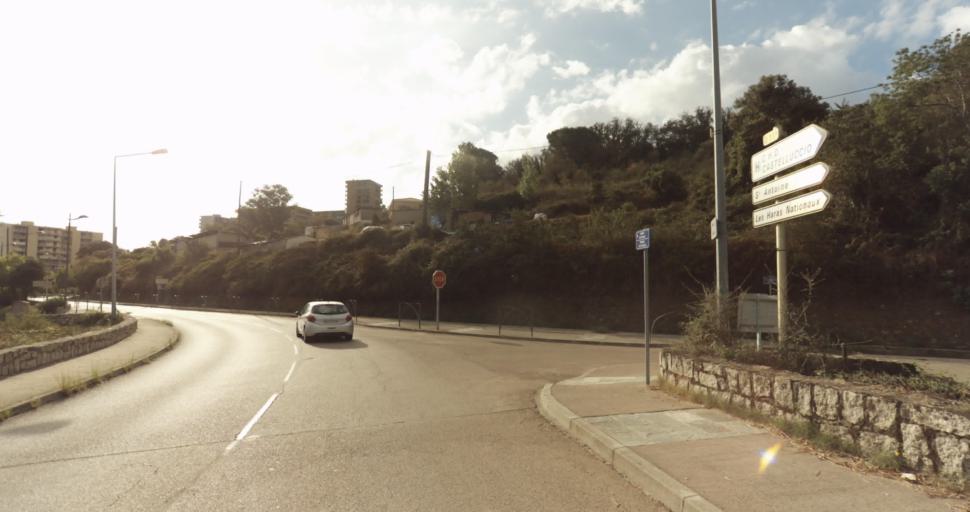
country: FR
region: Corsica
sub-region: Departement de la Corse-du-Sud
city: Ajaccio
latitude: 41.9293
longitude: 8.7264
